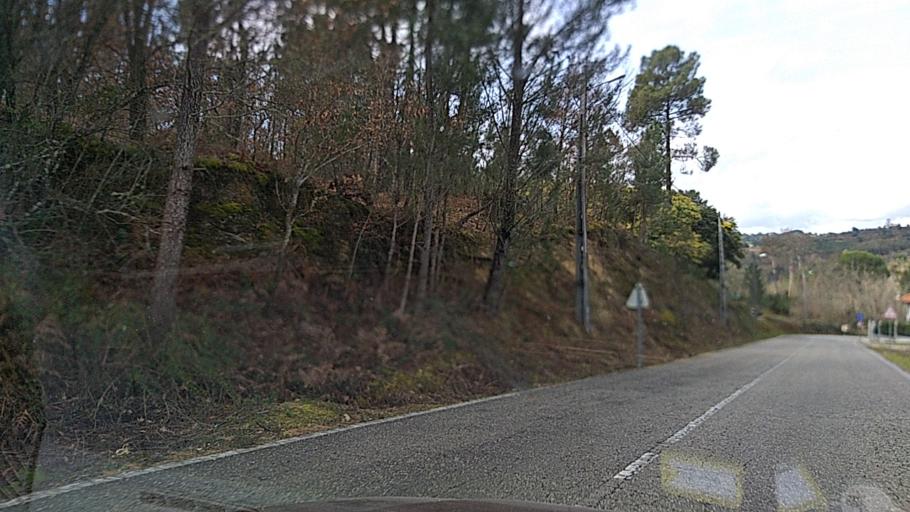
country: PT
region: Viseu
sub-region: Satao
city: Satao
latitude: 40.6651
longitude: -7.6798
